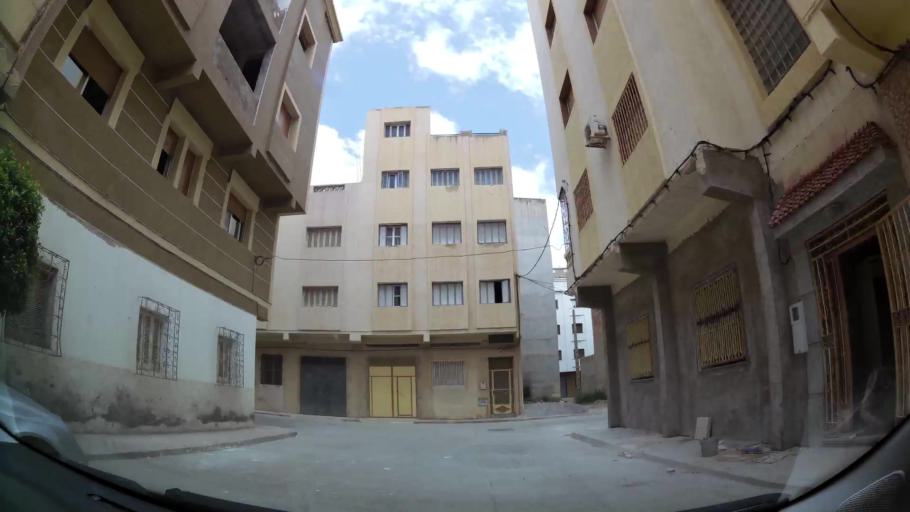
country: MA
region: Oriental
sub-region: Nador
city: Nador
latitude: 35.1671
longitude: -2.9246
